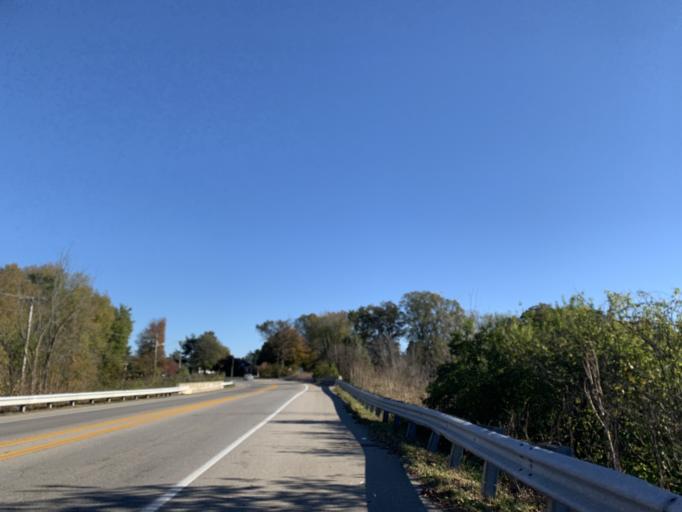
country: US
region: Kentucky
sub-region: Jefferson County
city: Pleasure Ridge Park
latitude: 38.1460
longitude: -85.8843
